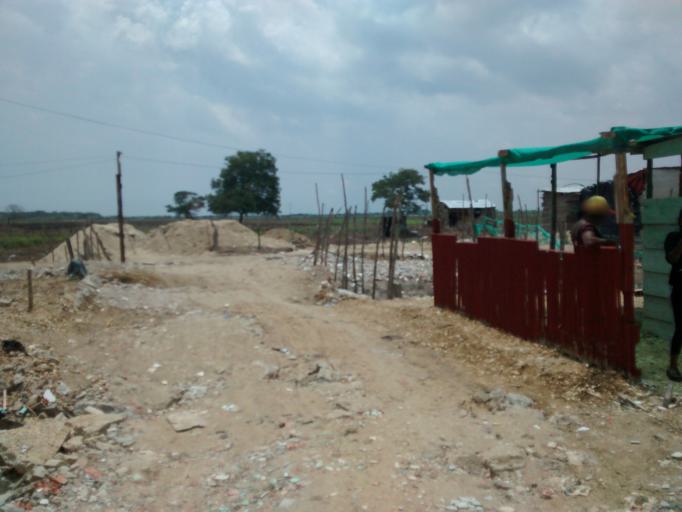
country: CO
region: Bolivar
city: Cartagena
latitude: 10.4153
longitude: -75.4685
